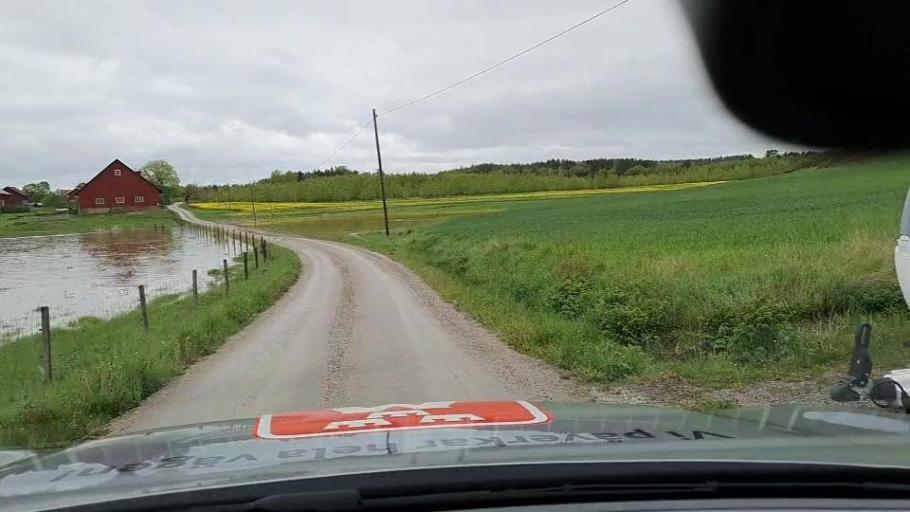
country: SE
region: Soedermanland
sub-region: Nykopings Kommun
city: Svalsta
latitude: 58.6419
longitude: 16.9334
